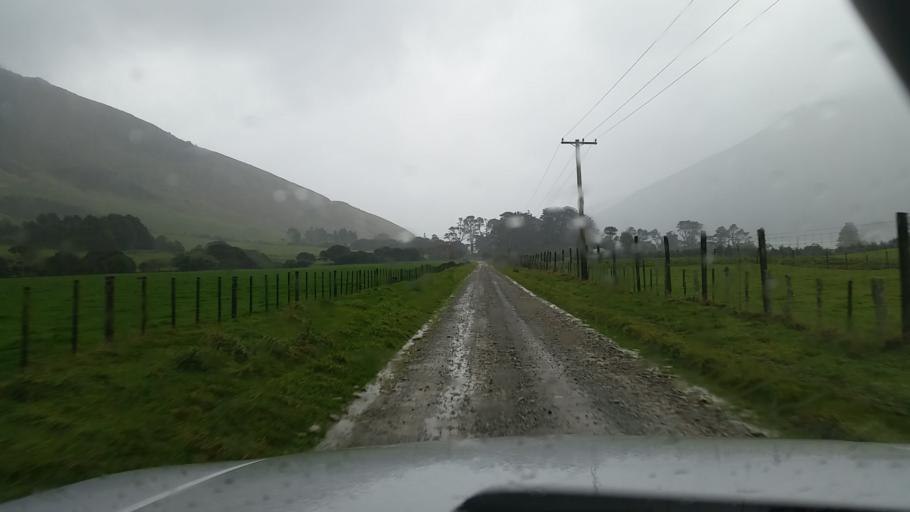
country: NZ
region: Marlborough
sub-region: Marlborough District
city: Picton
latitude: -41.1197
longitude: 174.0375
